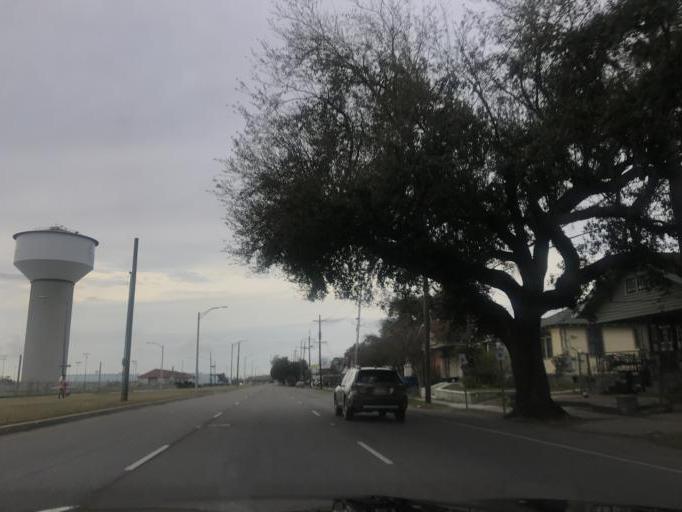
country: US
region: Louisiana
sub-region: Jefferson Parish
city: Jefferson
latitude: 29.9597
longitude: -90.1250
